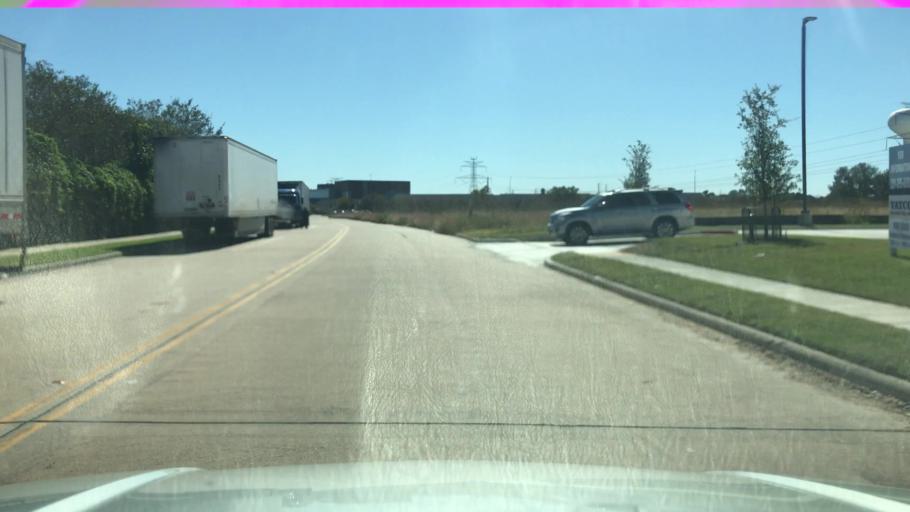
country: US
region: Texas
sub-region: Fort Bend County
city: Cinco Ranch
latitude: 29.7807
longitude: -95.7457
